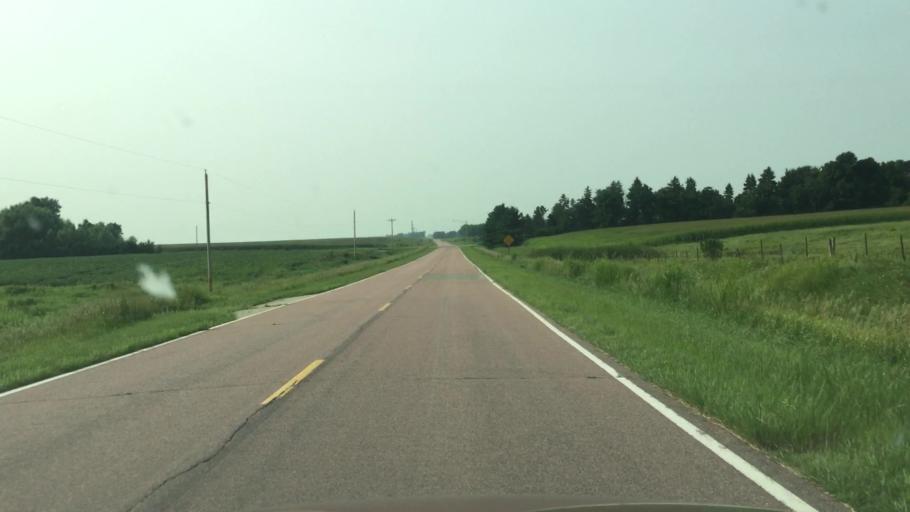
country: US
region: Iowa
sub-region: O'Brien County
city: Sheldon
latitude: 43.2473
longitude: -95.7833
